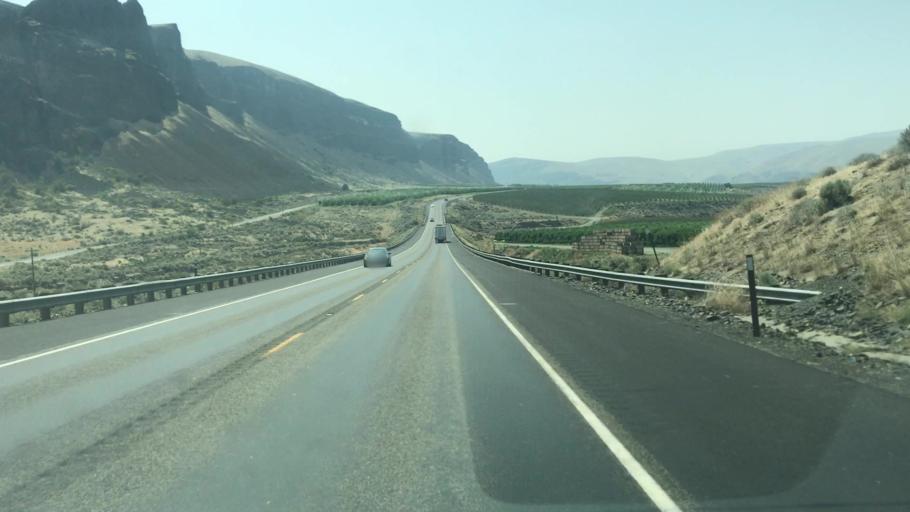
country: US
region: Washington
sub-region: Grant County
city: Quincy
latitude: 47.2851
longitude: -120.0656
